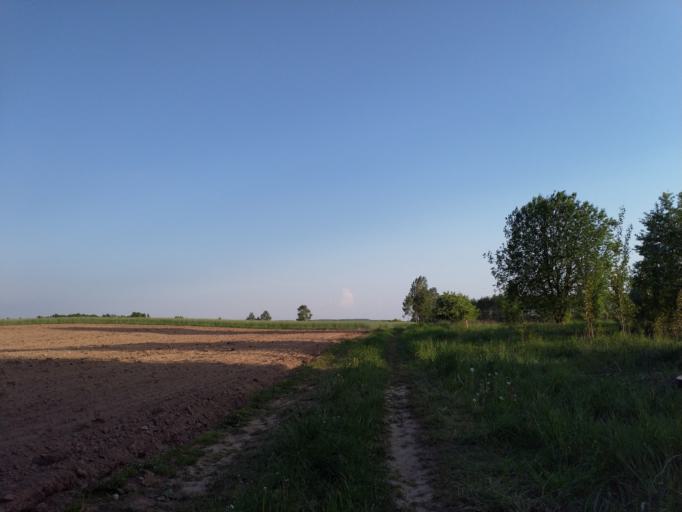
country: LV
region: Aizpute
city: Aizpute
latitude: 56.8315
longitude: 21.7825
